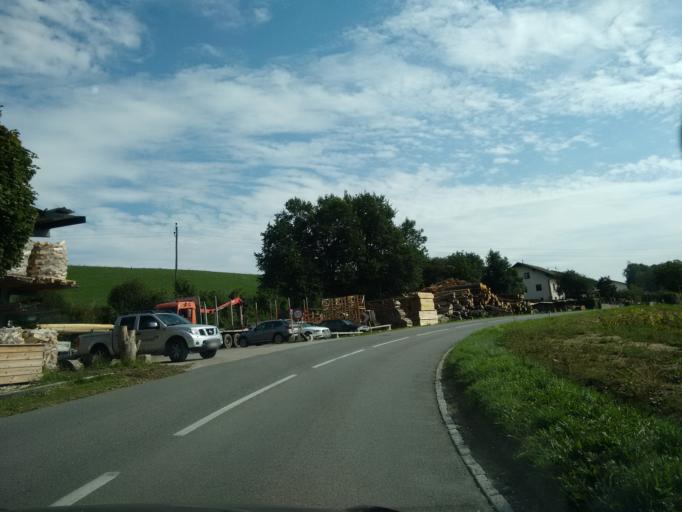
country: AT
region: Upper Austria
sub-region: Wels-Land
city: Thalheim bei Wels
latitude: 48.1437
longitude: 14.0482
